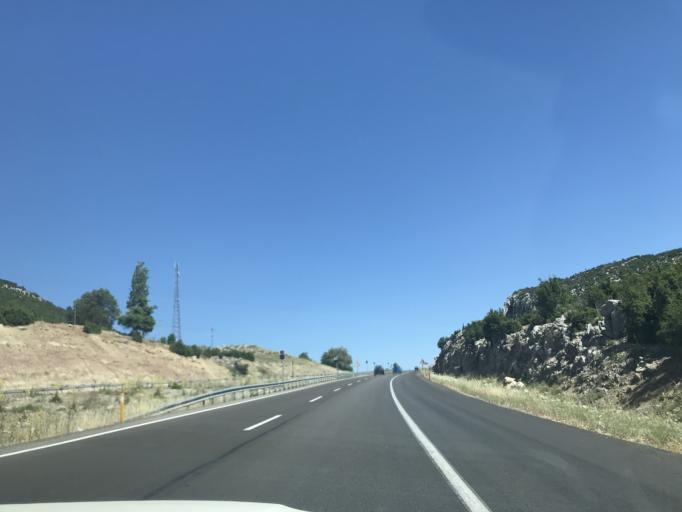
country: TR
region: Antalya
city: Dagbeli
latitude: 37.1665
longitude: 30.4994
